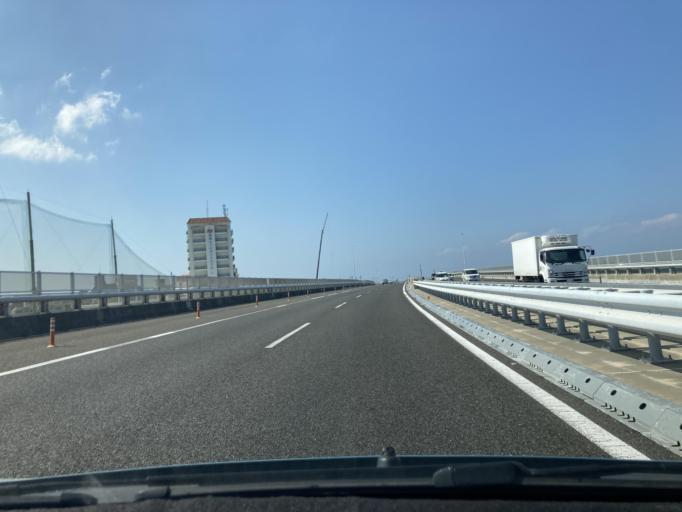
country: JP
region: Okinawa
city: Naha-shi
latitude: 26.2207
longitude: 127.6688
